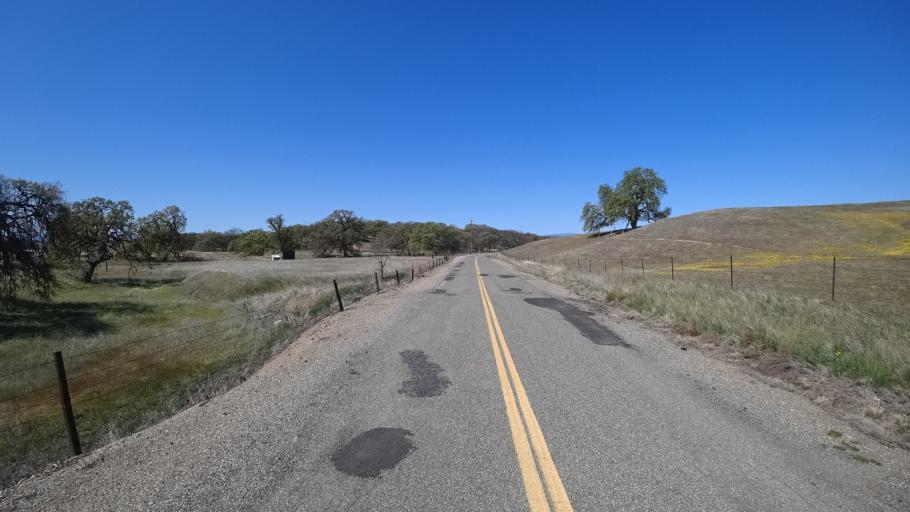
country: US
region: California
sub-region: Glenn County
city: Orland
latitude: 39.7628
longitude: -122.3411
